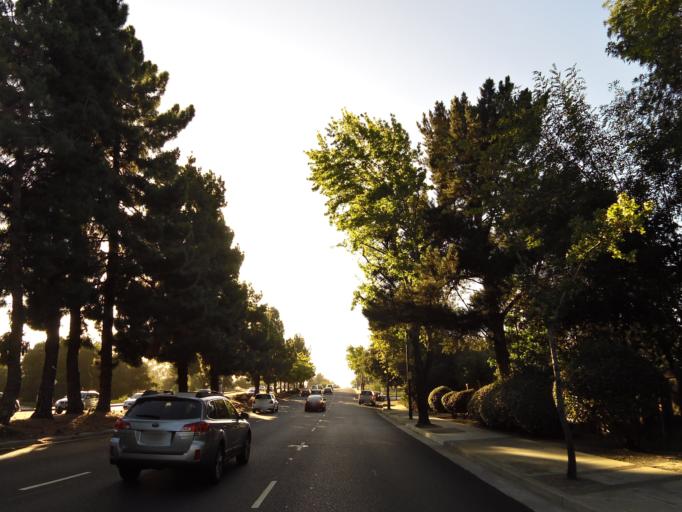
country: US
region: California
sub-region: Santa Clara County
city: Mountain View
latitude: 37.3773
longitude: -122.0649
